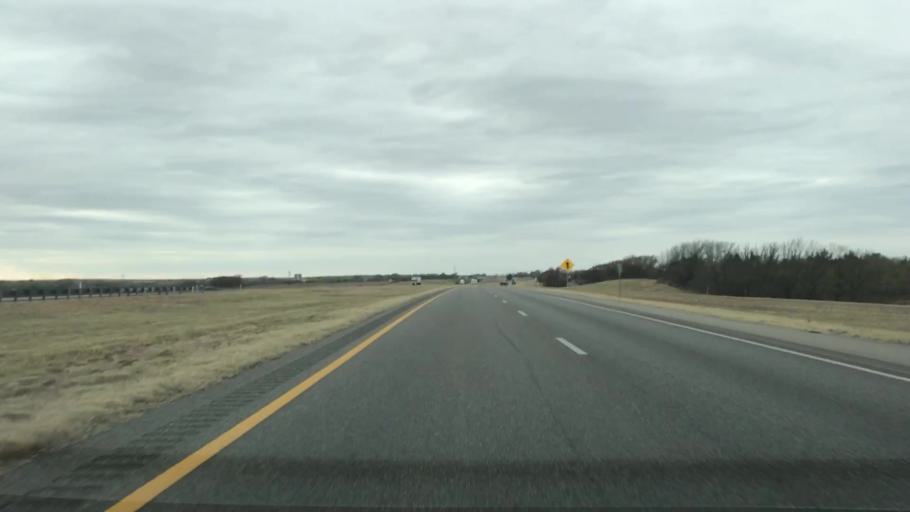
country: US
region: Oklahoma
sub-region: Beckham County
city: Erick
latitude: 35.2267
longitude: -99.9127
